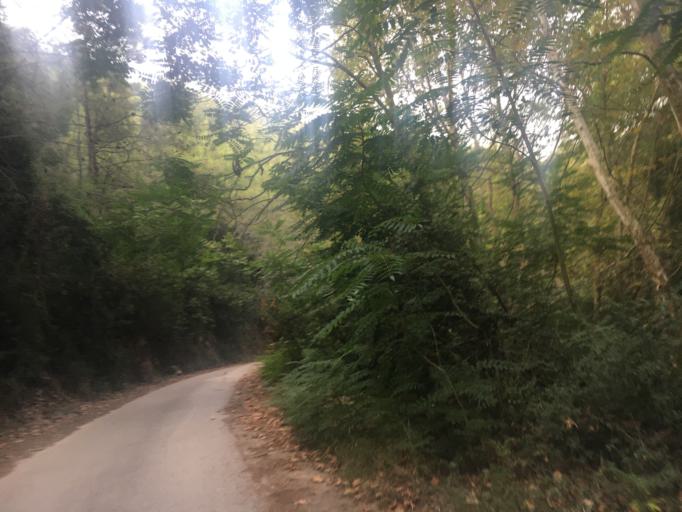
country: LB
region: Mont-Liban
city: Djounie
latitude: 33.9696
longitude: 35.6451
